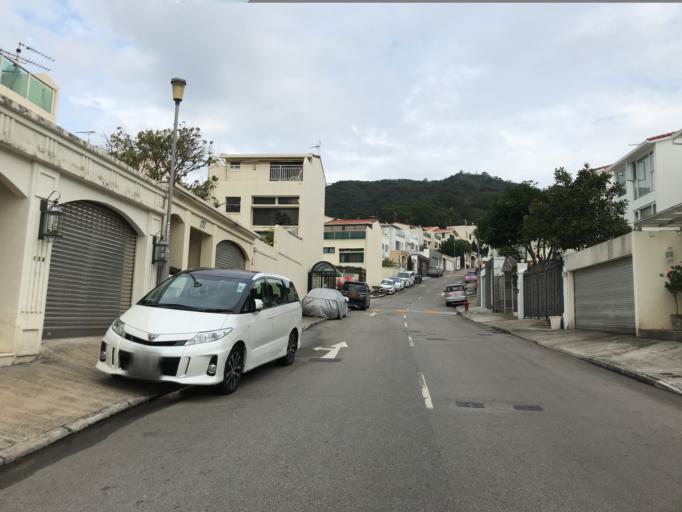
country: HK
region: Tai Po
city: Tai Po
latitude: 22.4654
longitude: 114.1563
